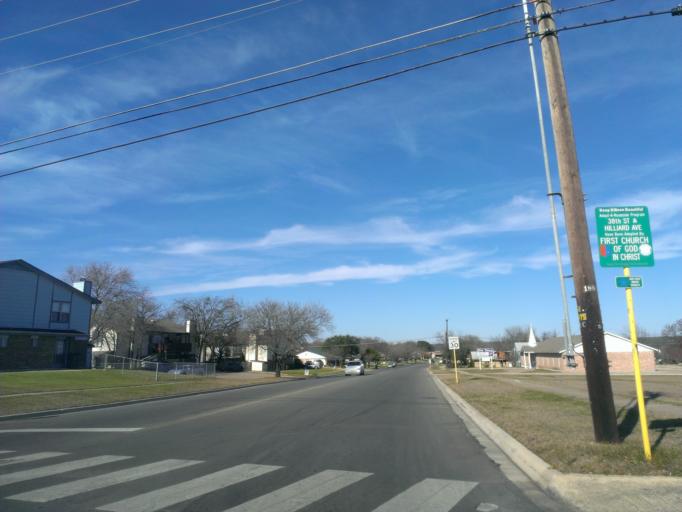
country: US
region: Texas
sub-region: Bell County
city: Killeen
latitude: 31.1238
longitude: -97.6963
